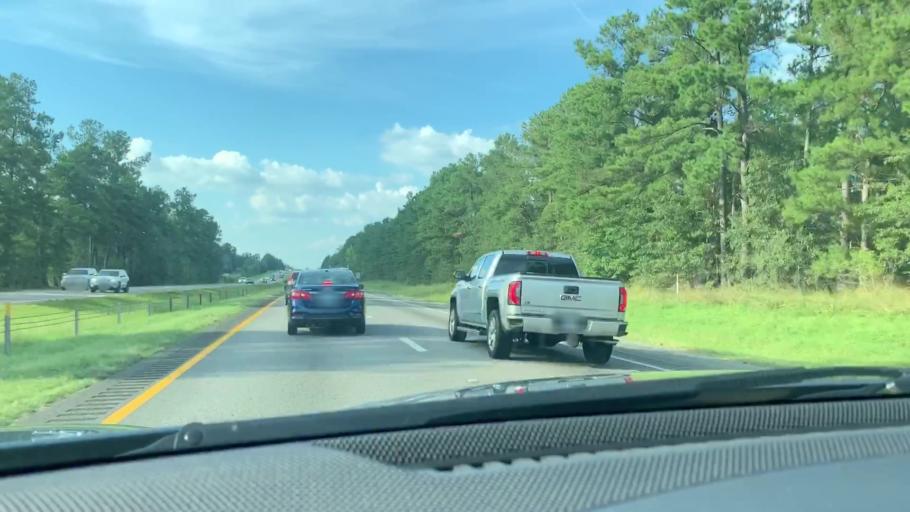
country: US
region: South Carolina
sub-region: Calhoun County
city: Saint Matthews
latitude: 33.6123
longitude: -80.8651
